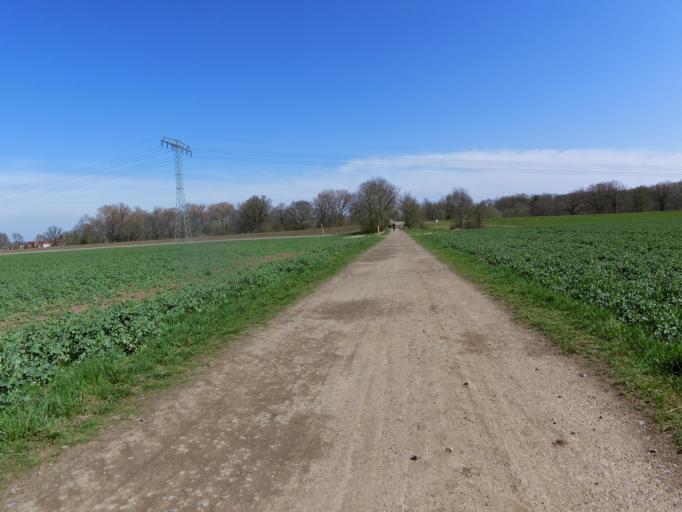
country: DE
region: Saxony
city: Schkeuditz
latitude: 51.3747
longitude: 12.2757
